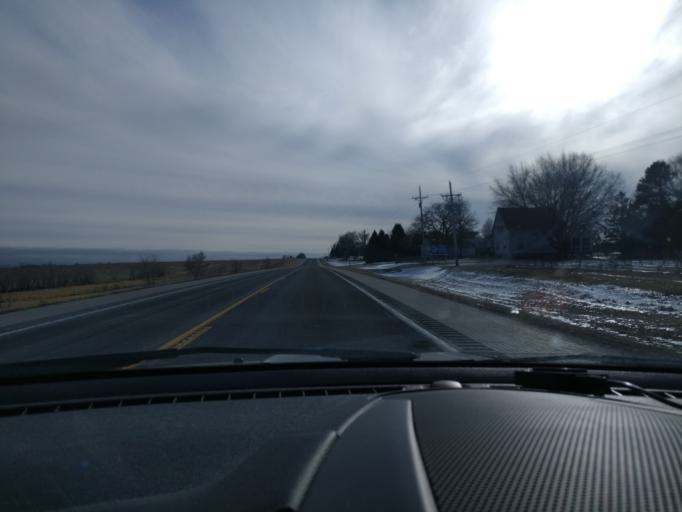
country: US
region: Nebraska
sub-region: Dodge County
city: Fremont
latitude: 41.3190
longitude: -96.5026
